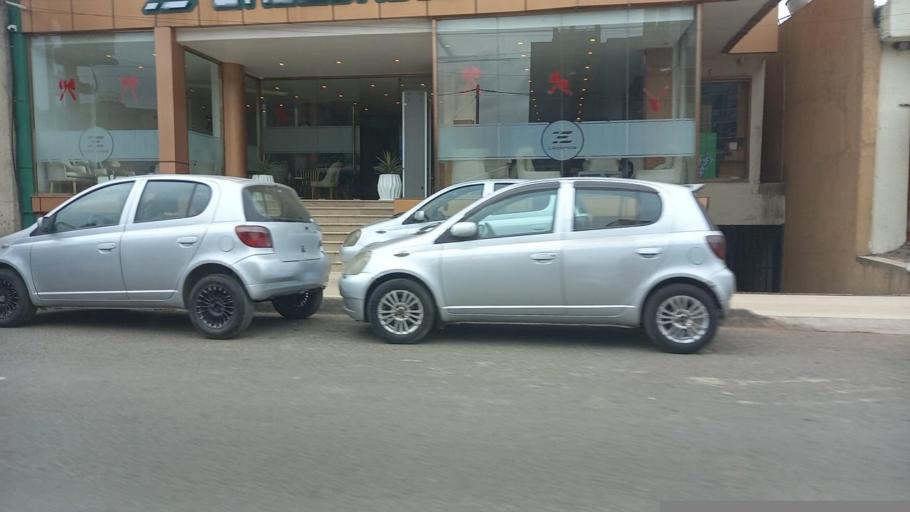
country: ET
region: Adis Abeba
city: Addis Ababa
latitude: 9.0109
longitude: 38.8375
